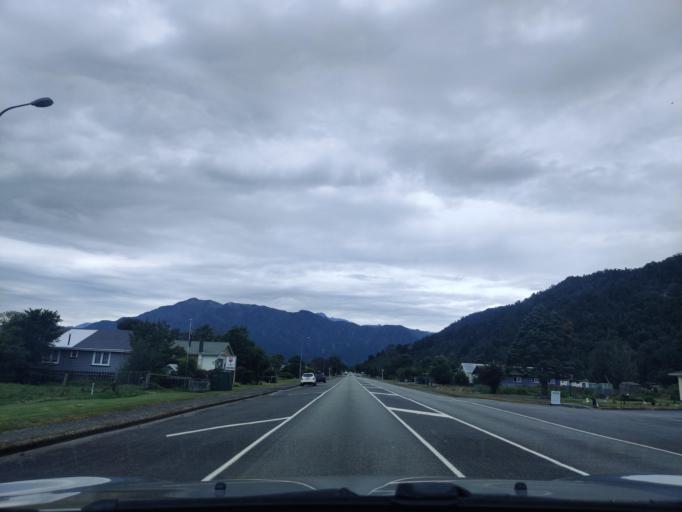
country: NZ
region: West Coast
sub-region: Westland District
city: Hokitika
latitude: -43.1494
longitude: 170.5585
